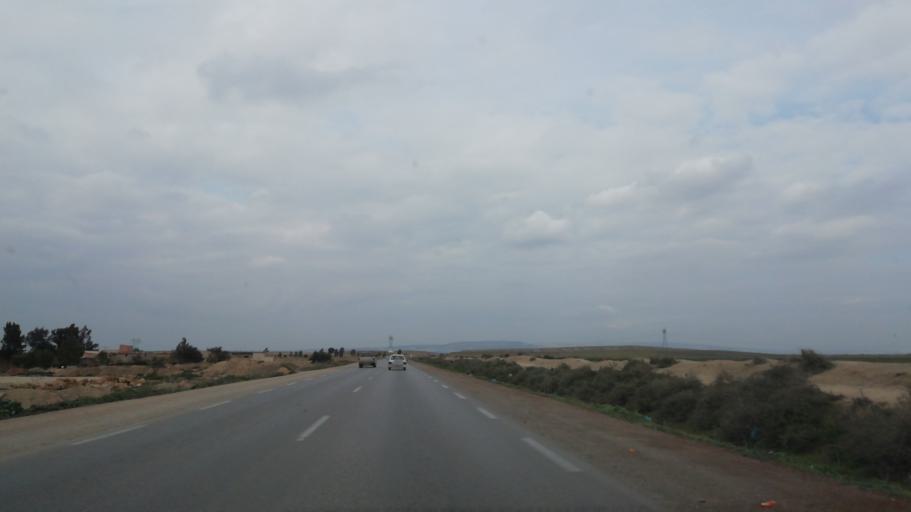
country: DZ
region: Mostaganem
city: Mostaganem
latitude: 35.7042
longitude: 0.0549
